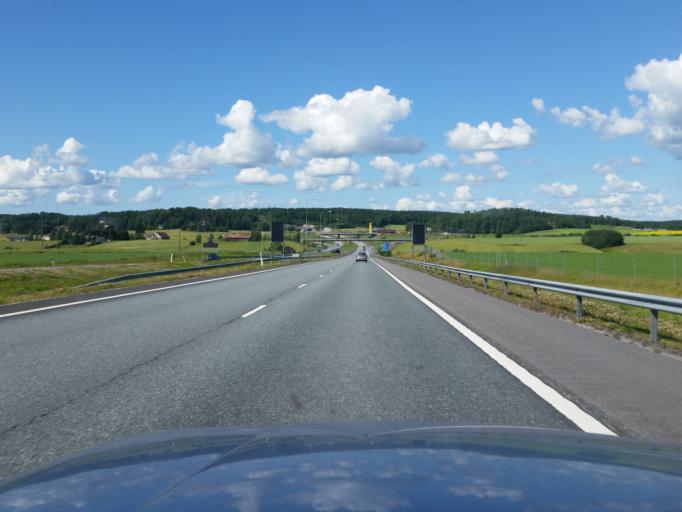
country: FI
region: Varsinais-Suomi
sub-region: Salo
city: Salo
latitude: 60.4135
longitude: 23.1859
